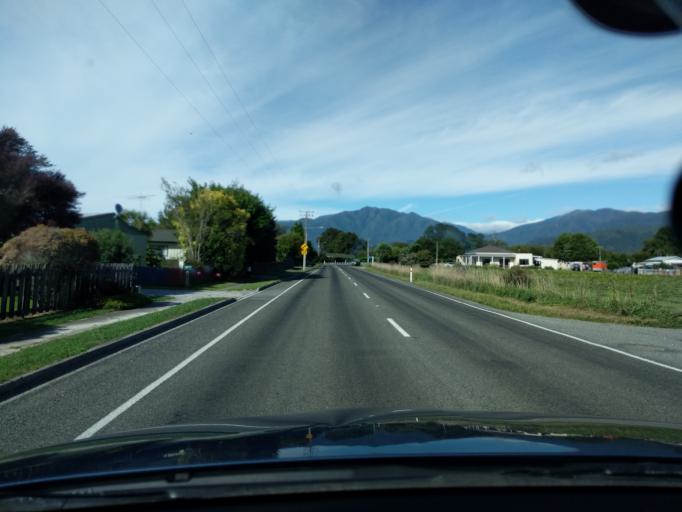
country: NZ
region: Tasman
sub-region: Tasman District
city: Takaka
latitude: -40.8569
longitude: 172.8226
